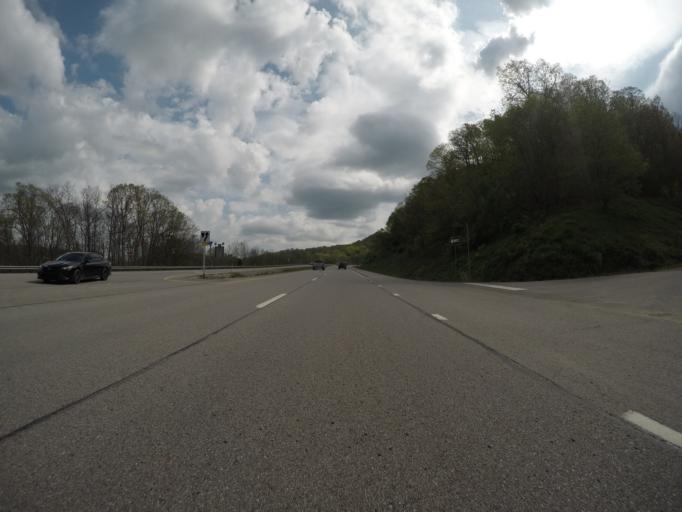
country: US
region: West Virginia
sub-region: Kanawha County
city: Alum Creek
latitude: 38.2664
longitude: -81.8280
